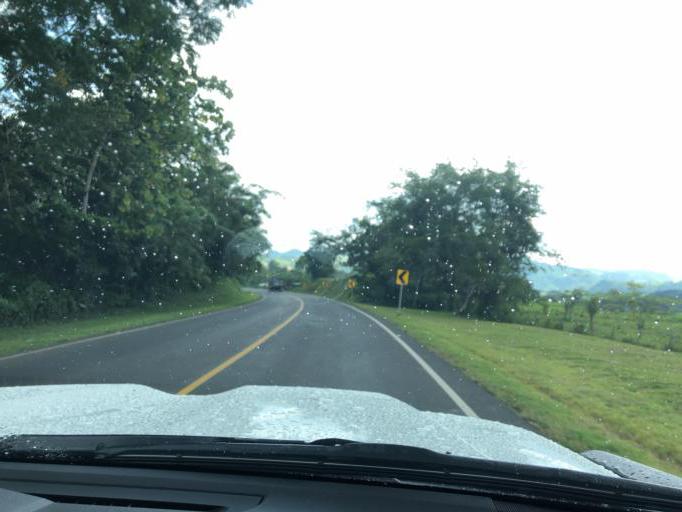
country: NI
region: Chontales
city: Villa Sandino
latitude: 12.0085
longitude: -84.9442
